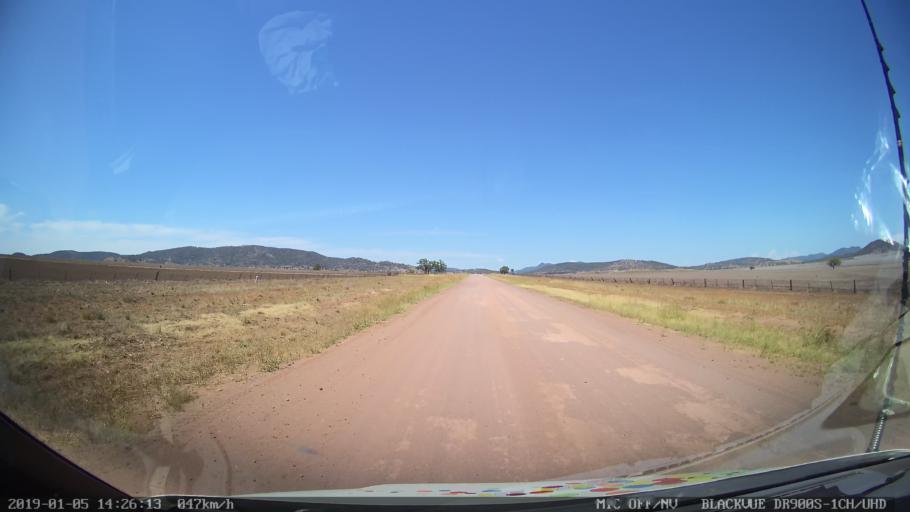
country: AU
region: New South Wales
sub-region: Liverpool Plains
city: Quirindi
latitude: -31.2384
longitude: 150.5555
